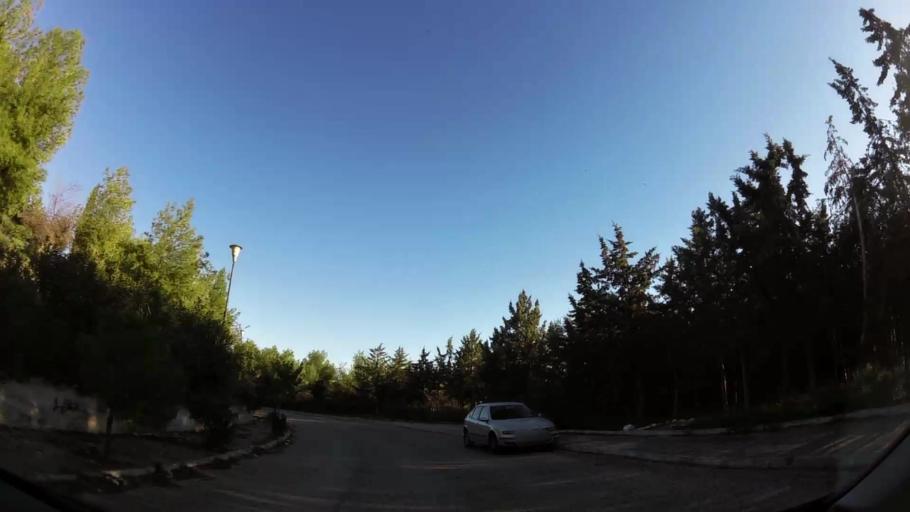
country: GR
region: Attica
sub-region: Nomarchia Anatolikis Attikis
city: Acharnes
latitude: 38.0822
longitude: 23.7223
